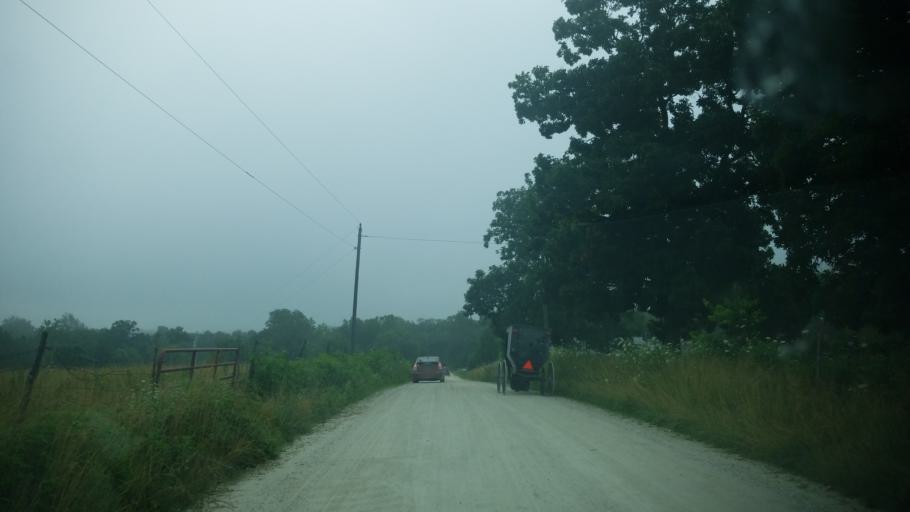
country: US
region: Missouri
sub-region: Pike County
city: Bowling Green
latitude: 39.3082
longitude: -91.2964
